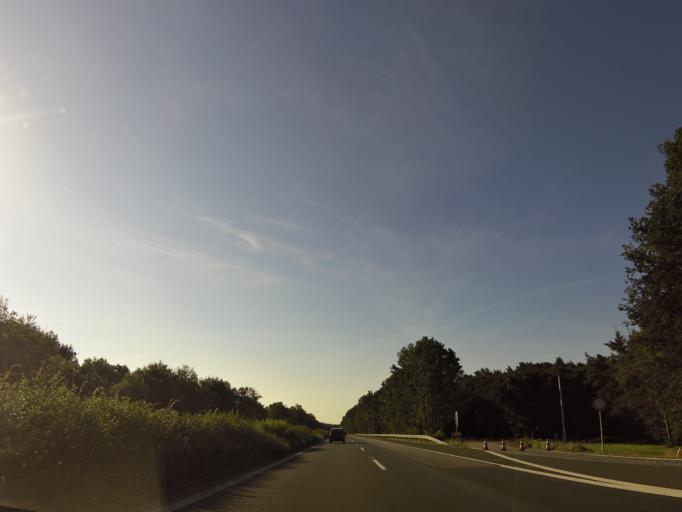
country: DE
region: Bavaria
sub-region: Regierungsbezirk Mittelfranken
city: Grossenseebach
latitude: 49.6698
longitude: 10.8782
